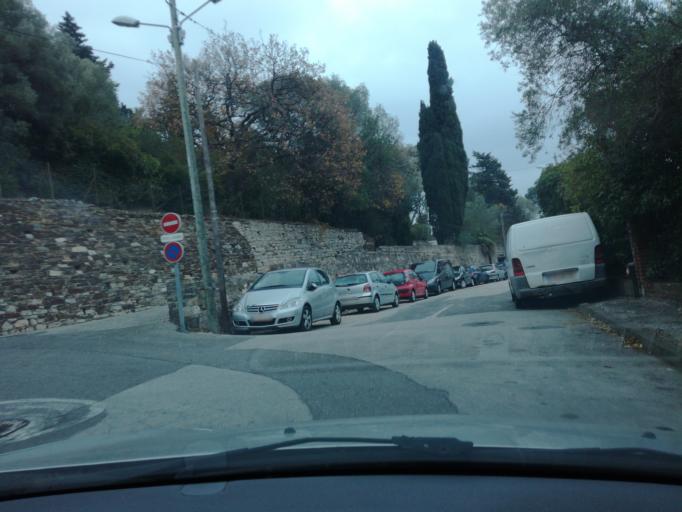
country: FR
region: Provence-Alpes-Cote d'Azur
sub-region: Departement du Var
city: Hyeres
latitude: 43.1212
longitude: 6.1232
